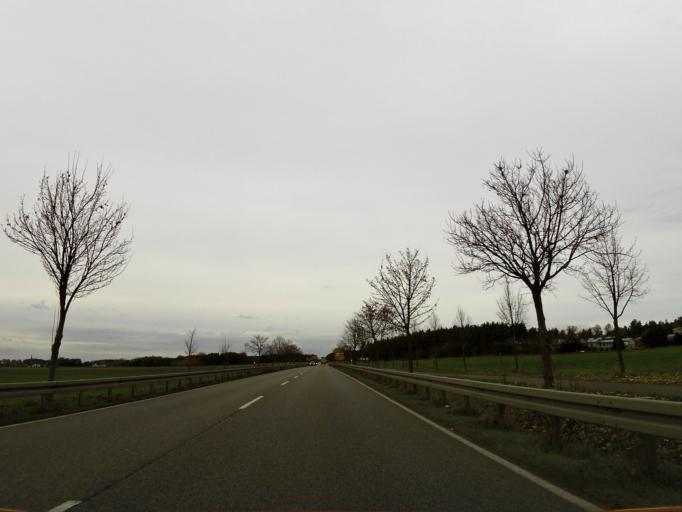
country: DE
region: Saxony-Anhalt
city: Salzwedel
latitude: 52.8246
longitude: 11.1995
